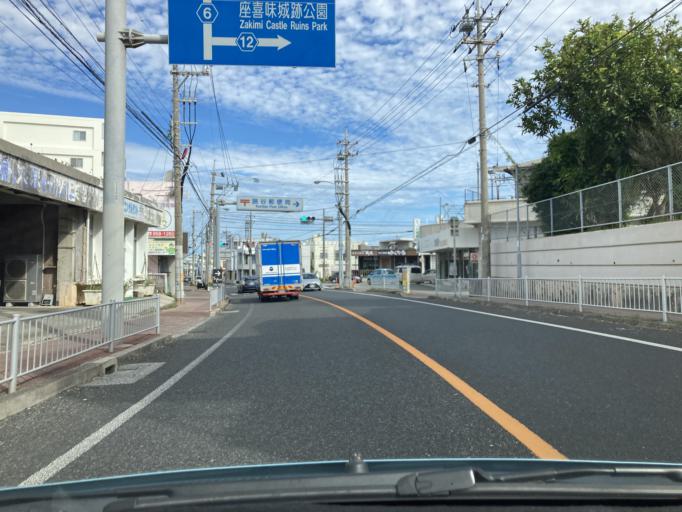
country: JP
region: Okinawa
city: Ishikawa
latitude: 26.4077
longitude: 127.7321
